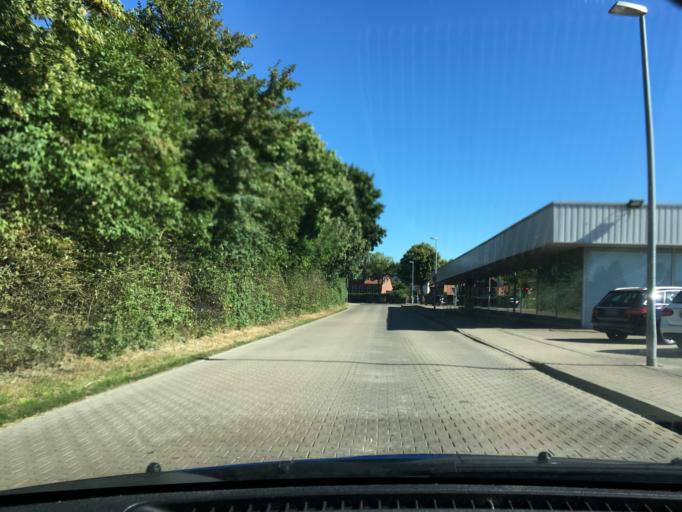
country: DE
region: Lower Saxony
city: Wendisch Evern
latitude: 53.2418
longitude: 10.4522
